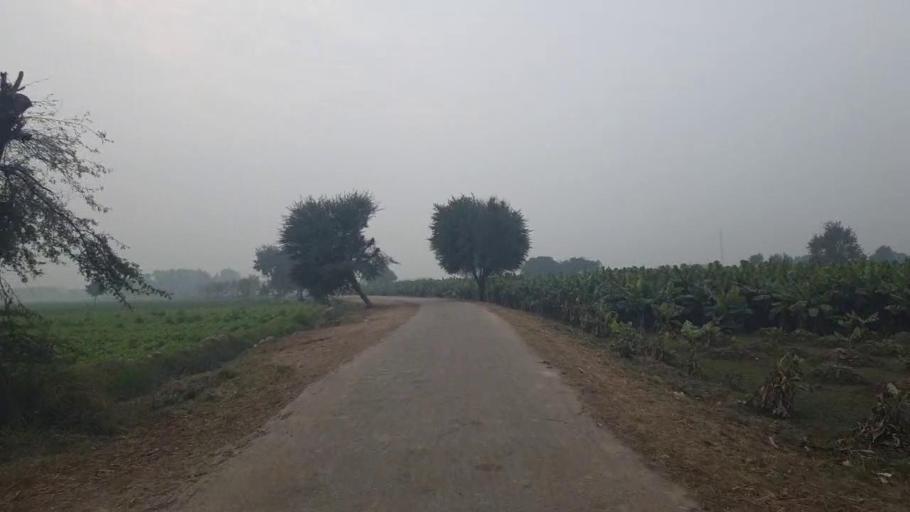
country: PK
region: Sindh
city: Tando Adam
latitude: 25.7365
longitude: 68.6696
